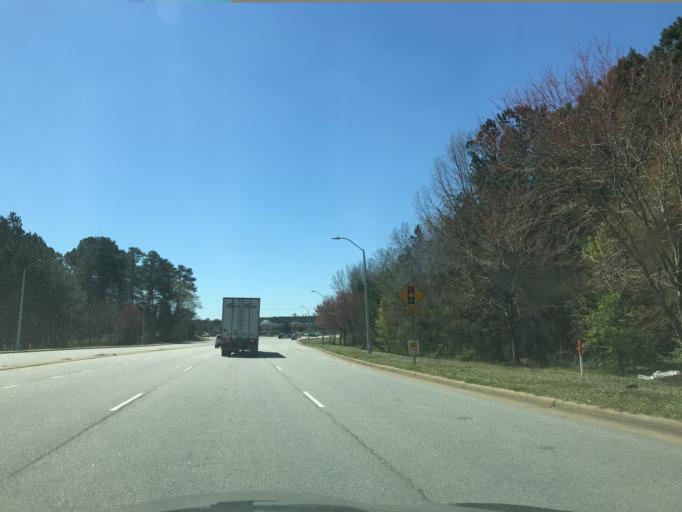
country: US
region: North Carolina
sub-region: Wake County
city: Garner
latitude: 35.7214
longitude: -78.6384
